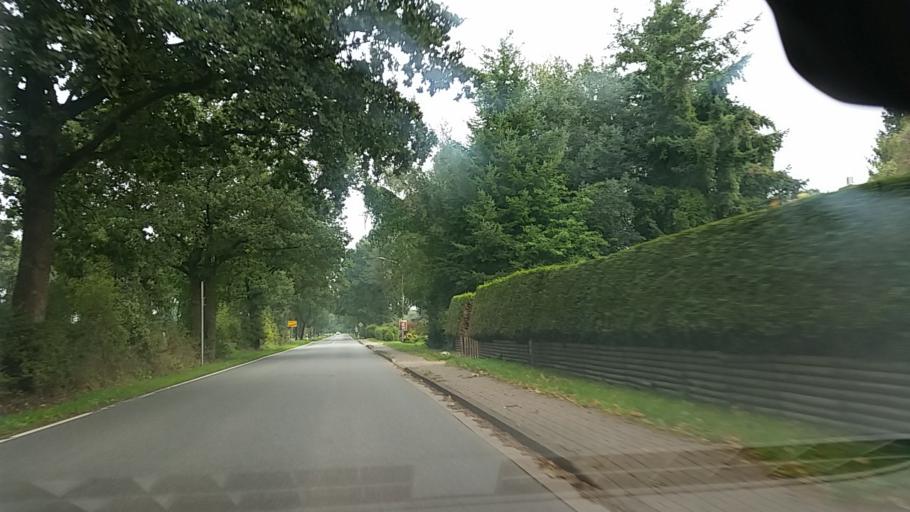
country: DE
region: Schleswig-Holstein
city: Hasenmoor
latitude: 53.8845
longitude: 9.9829
